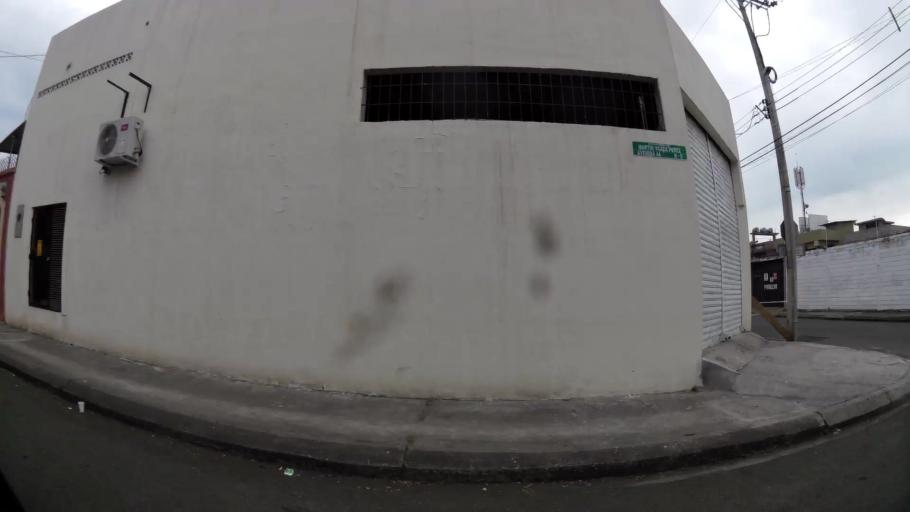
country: EC
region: Guayas
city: Eloy Alfaro
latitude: -2.1321
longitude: -79.8862
